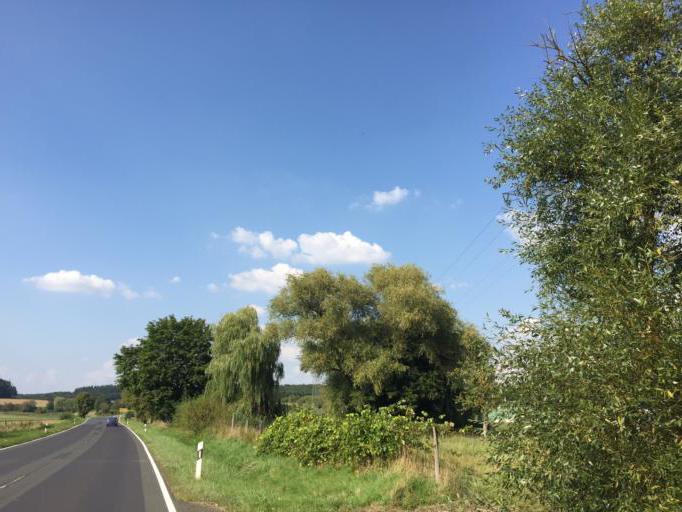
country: DE
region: Hesse
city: Staufenberg
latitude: 50.6632
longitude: 8.7177
